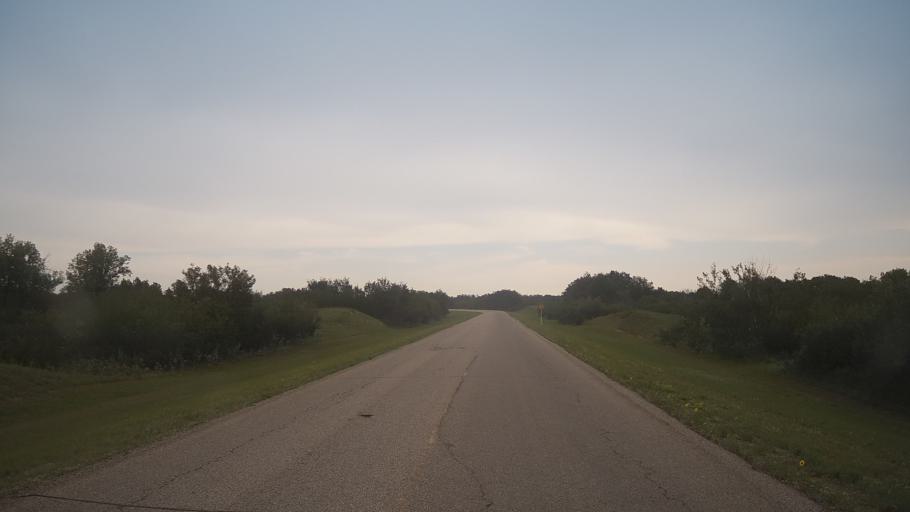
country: CA
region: Saskatchewan
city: Saskatoon
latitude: 51.8455
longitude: -106.5419
